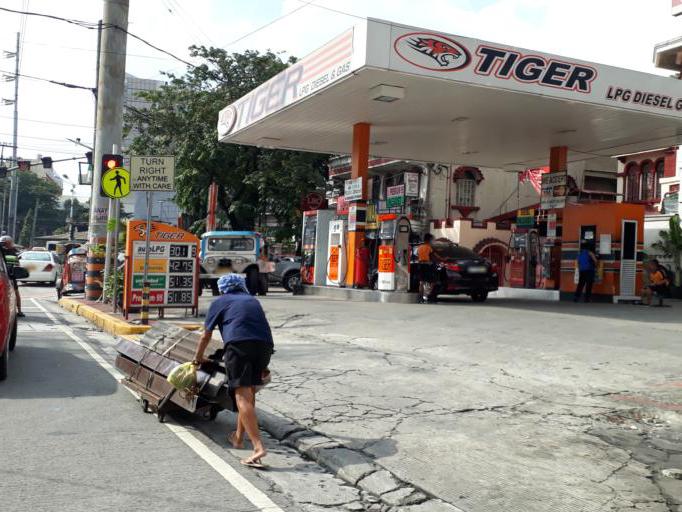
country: PH
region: Metro Manila
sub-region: City of Manila
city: Manila
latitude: 14.6232
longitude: 120.9894
